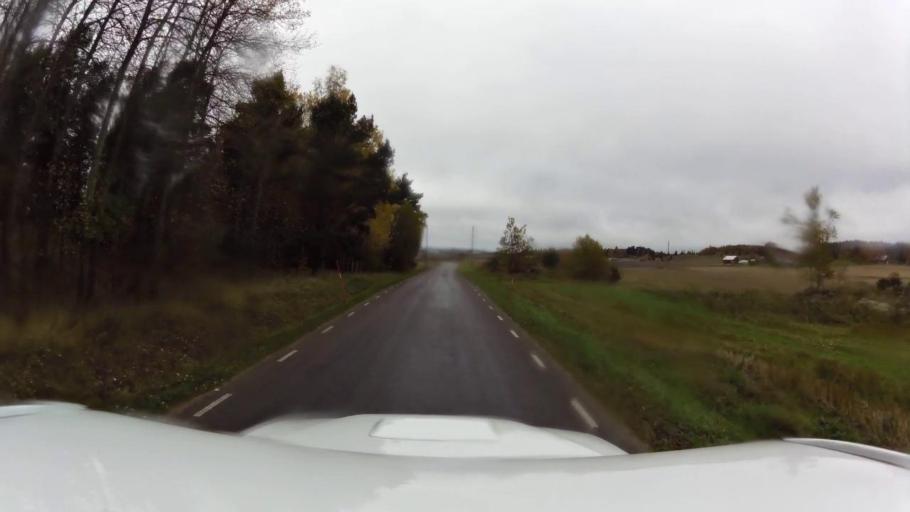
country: SE
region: OEstergoetland
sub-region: Linkopings Kommun
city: Linghem
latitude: 58.4660
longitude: 15.8257
